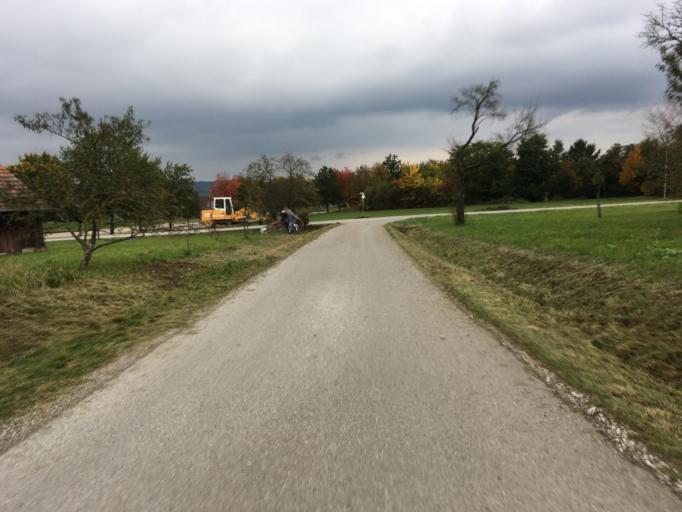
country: DE
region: Baden-Wuerttemberg
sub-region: Tuebingen Region
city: Gomaringen
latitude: 48.4460
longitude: 9.0910
